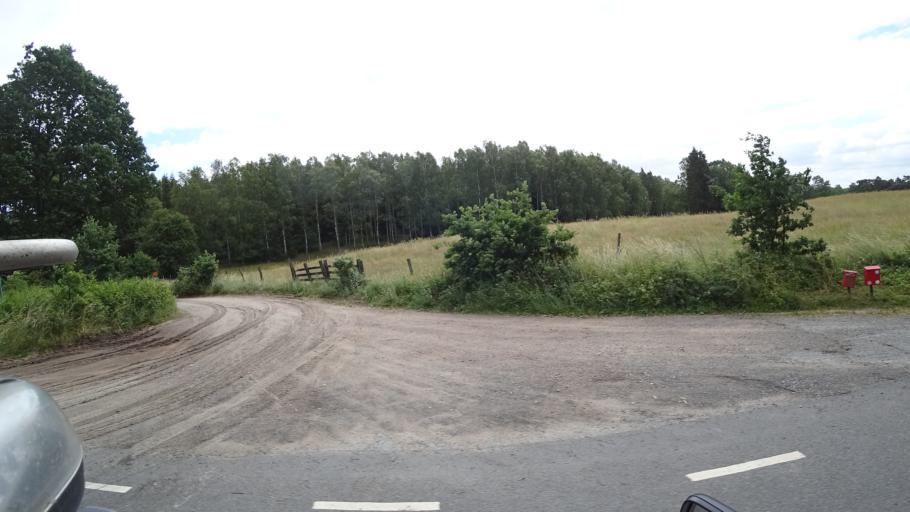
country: SE
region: Skane
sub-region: Kristianstads Kommun
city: Degeberga
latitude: 55.7169
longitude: 13.9893
